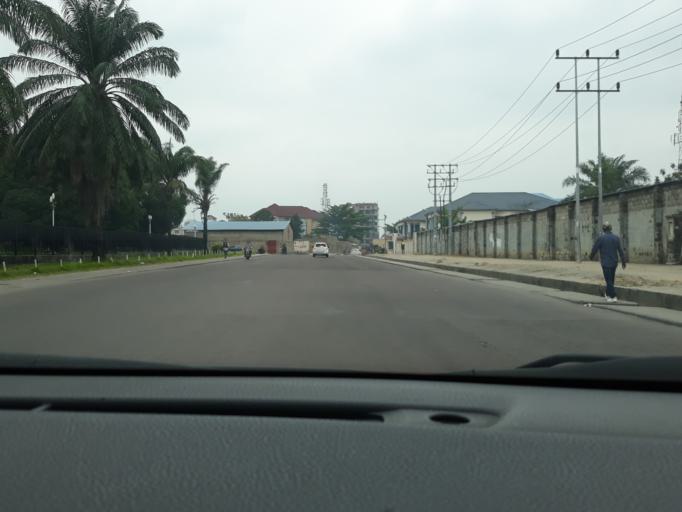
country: CD
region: Kinshasa
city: Kinshasa
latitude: -4.3311
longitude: 15.3053
